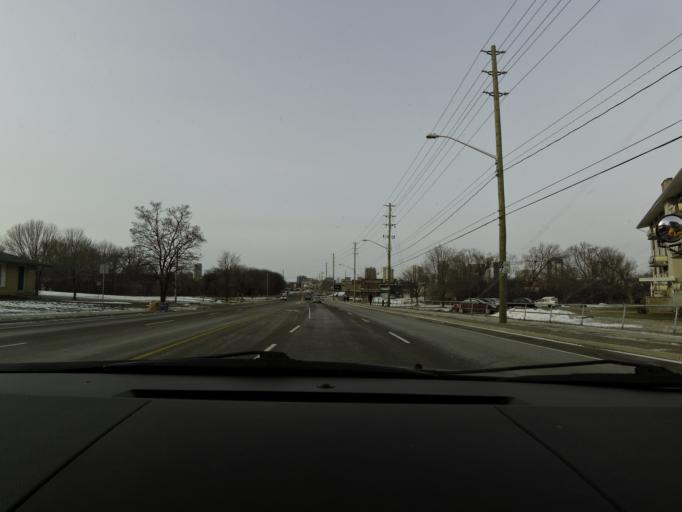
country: CA
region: Ontario
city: Waterloo
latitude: 43.4807
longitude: -80.5136
